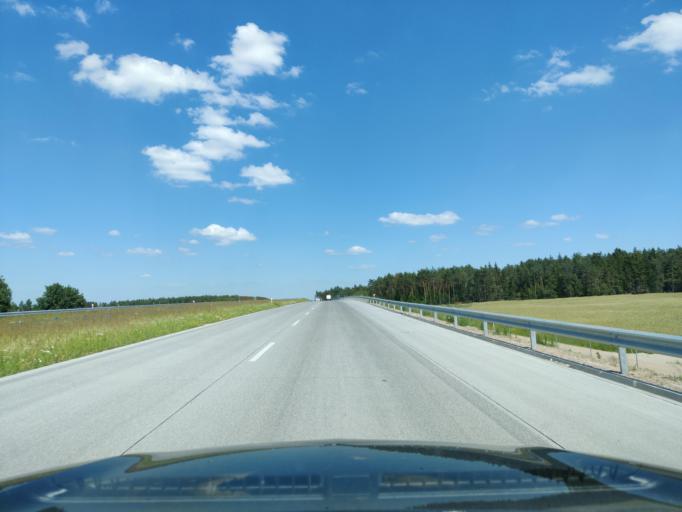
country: PL
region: Masovian Voivodeship
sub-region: Powiat mlawski
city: Wisniewo
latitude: 52.9782
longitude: 20.3343
